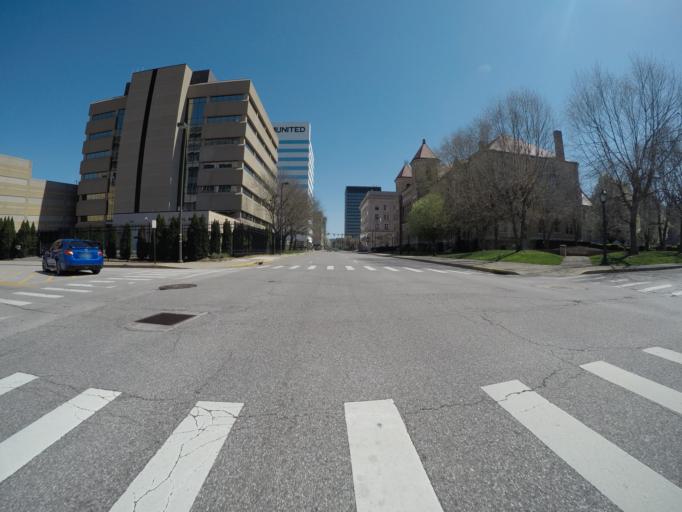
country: US
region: West Virginia
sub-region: Kanawha County
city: Charleston
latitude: 38.3519
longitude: -81.6391
